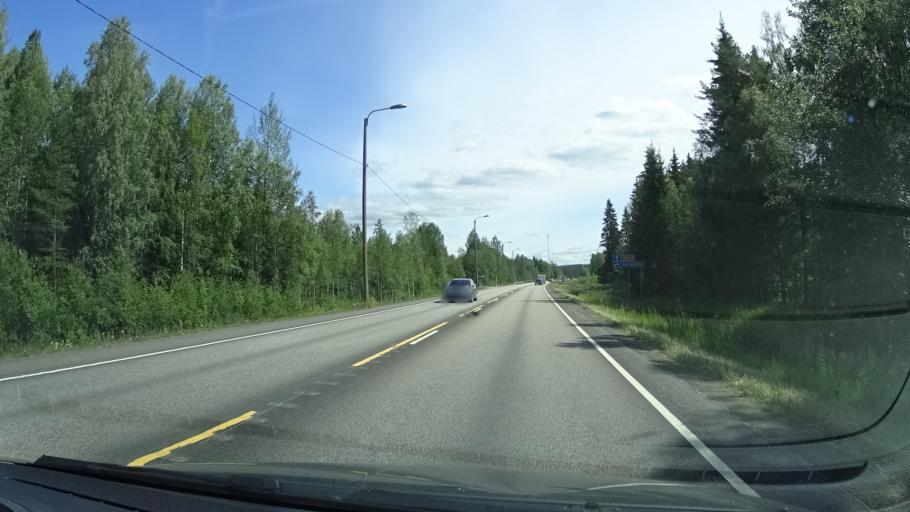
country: FI
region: Central Finland
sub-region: Jyvaeskylae
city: Uurainen
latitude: 62.2656
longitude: 25.4544
